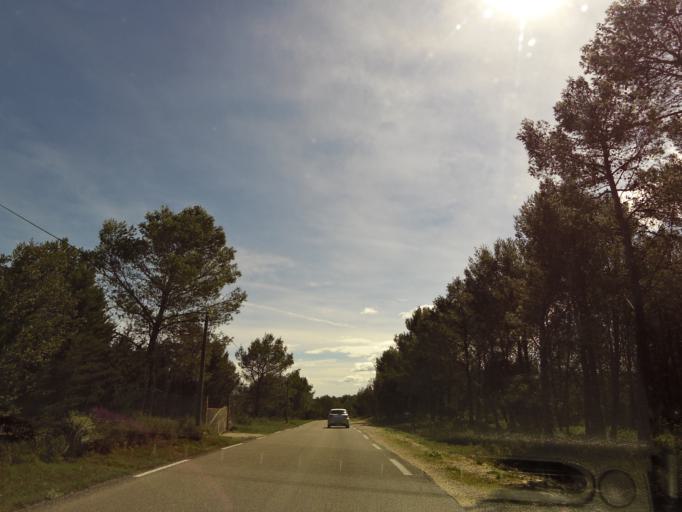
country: FR
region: Languedoc-Roussillon
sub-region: Departement du Gard
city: Langlade
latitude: 43.7931
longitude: 4.2590
